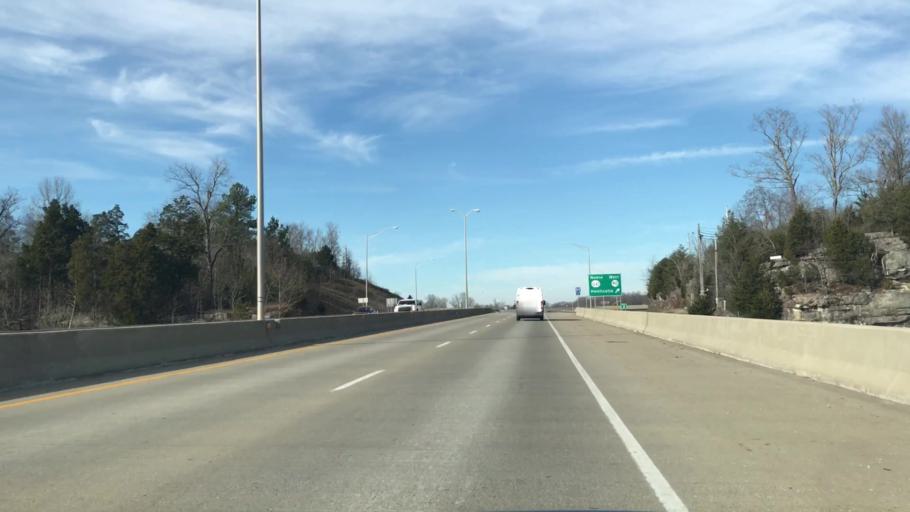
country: US
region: Kentucky
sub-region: Pulaski County
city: Somerset
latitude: 36.9964
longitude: -84.6071
